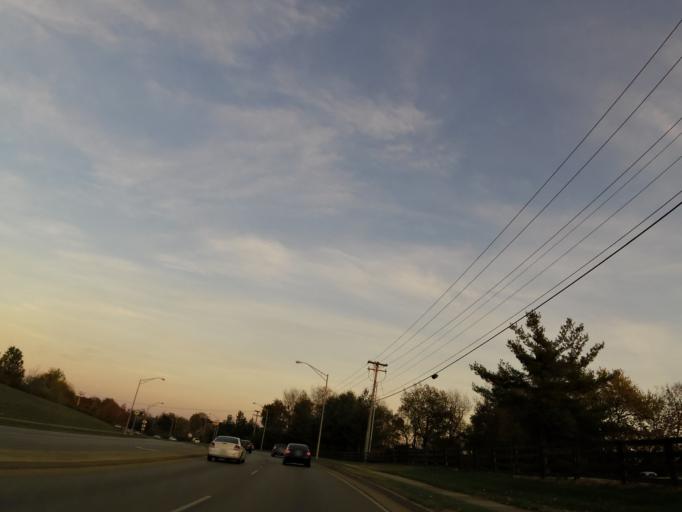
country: US
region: Kentucky
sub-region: Fayette County
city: Lexington
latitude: 37.9647
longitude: -84.4818
